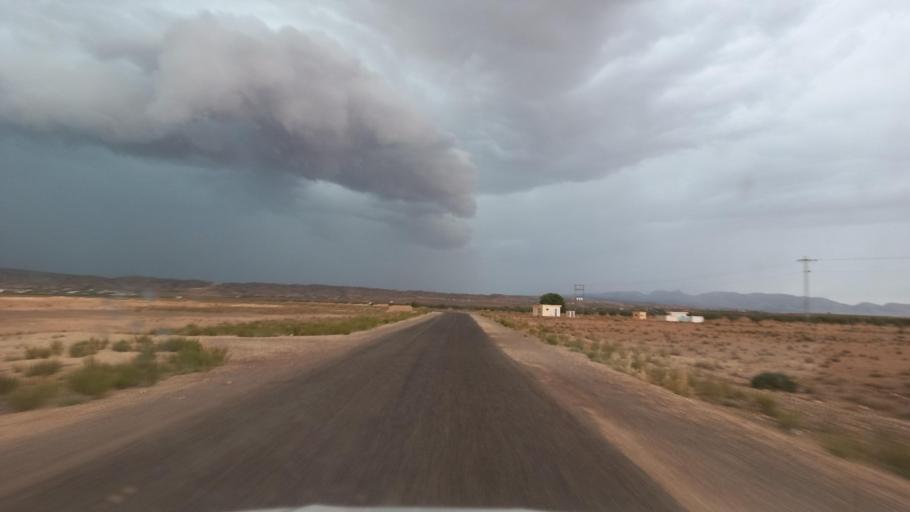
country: TN
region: Al Qasrayn
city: Sbiba
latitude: 35.3252
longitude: 9.0145
